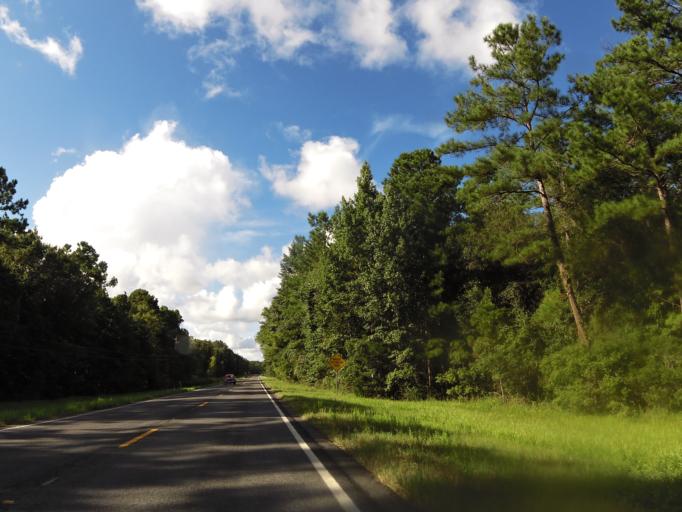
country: US
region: Georgia
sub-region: Camden County
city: Woodbine
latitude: 30.9952
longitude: -81.7304
